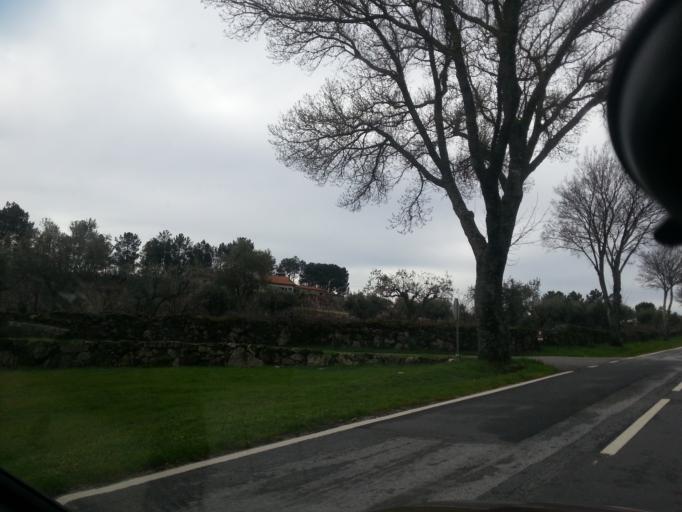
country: PT
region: Guarda
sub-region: Fornos de Algodres
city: Fornos de Algodres
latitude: 40.5279
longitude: -7.5885
